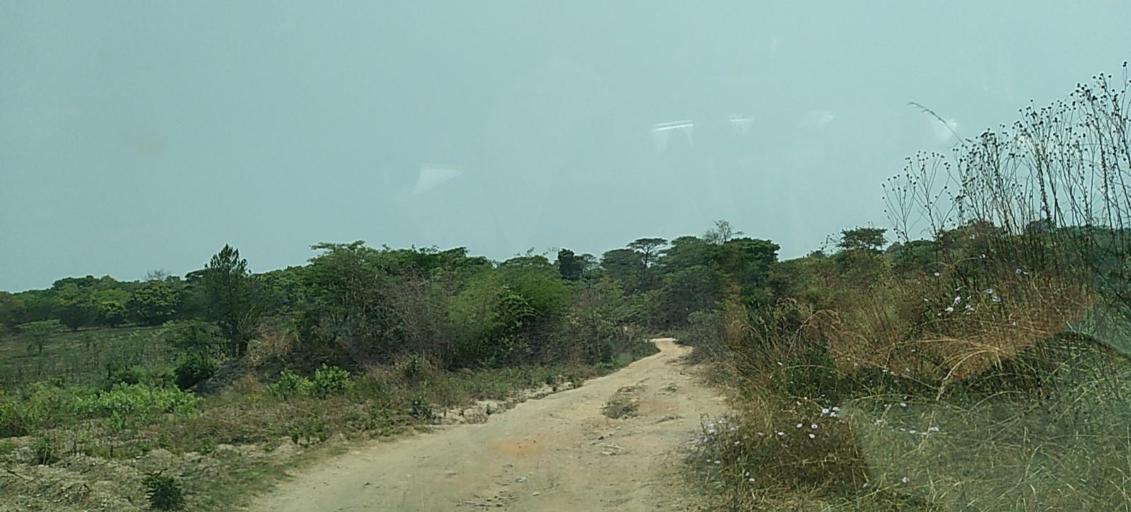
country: ZM
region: Copperbelt
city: Kalulushi
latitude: -12.9561
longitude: 28.1488
